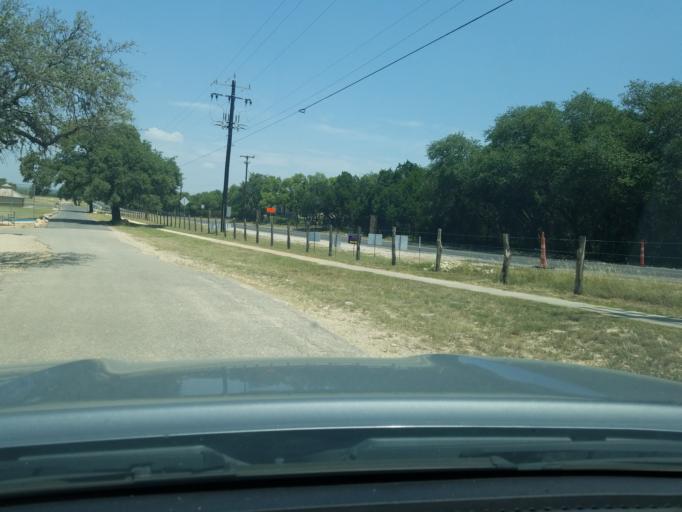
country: US
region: Texas
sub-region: Bexar County
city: Timberwood Park
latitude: 29.7083
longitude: -98.5131
